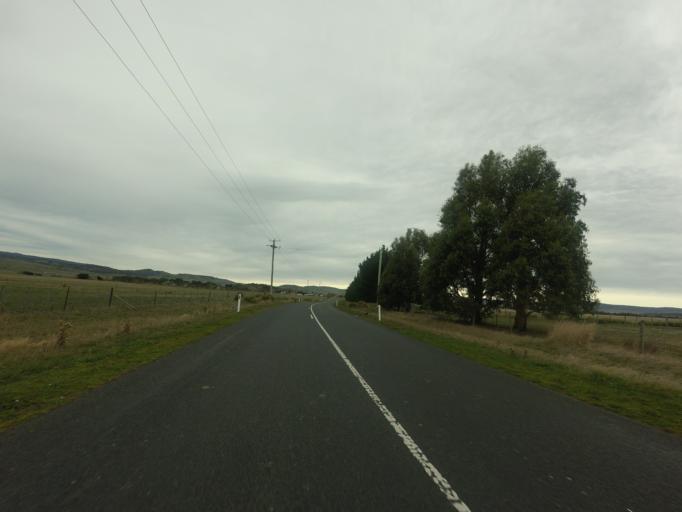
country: AU
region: Tasmania
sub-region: Derwent Valley
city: New Norfolk
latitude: -42.3976
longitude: 147.0055
